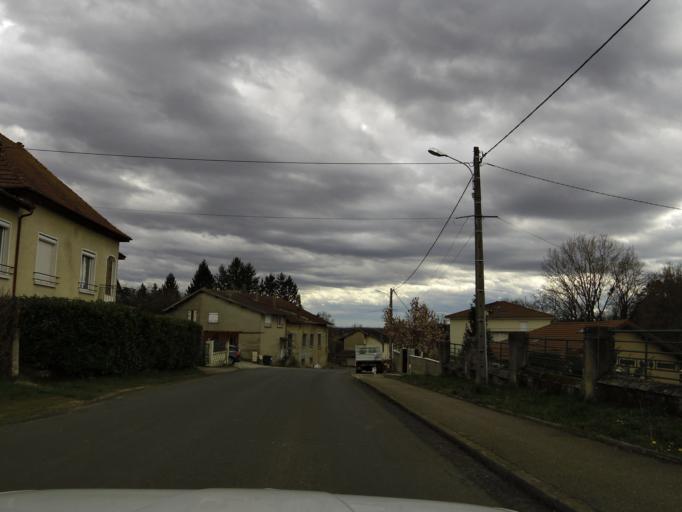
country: FR
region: Rhone-Alpes
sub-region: Departement de l'Ain
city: Meximieux
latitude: 45.9240
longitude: 5.2260
